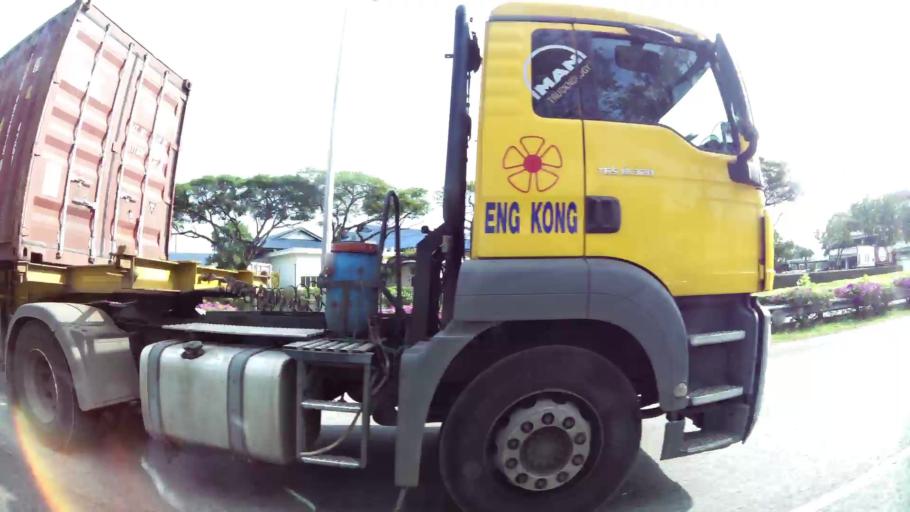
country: MY
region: Johor
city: Johor Bahru
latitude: 1.3345
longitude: 103.6515
